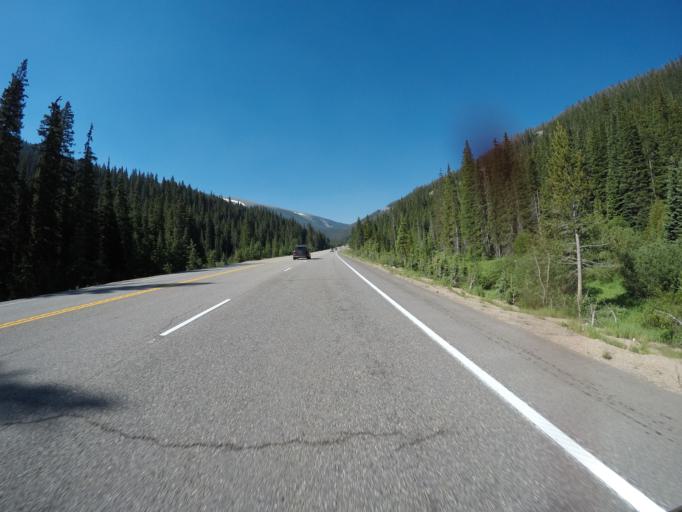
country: US
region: Colorado
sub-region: Grand County
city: Fraser
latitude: 39.8388
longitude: -105.7543
